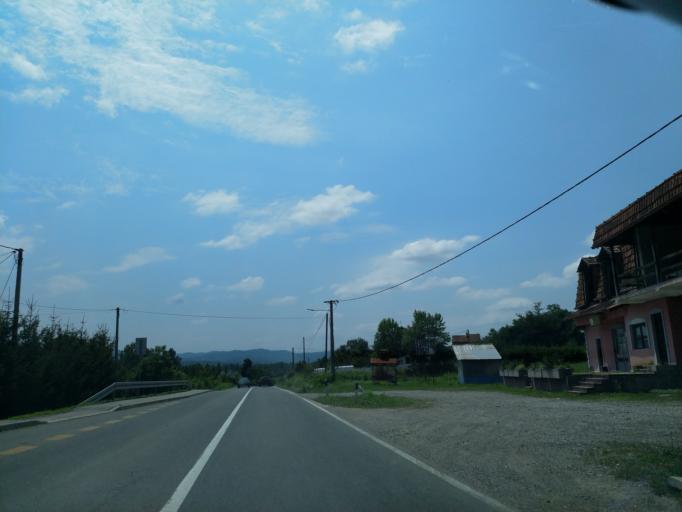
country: RS
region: Central Serbia
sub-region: Rasinski Okrug
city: Krusevac
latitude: 43.4893
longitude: 21.2793
